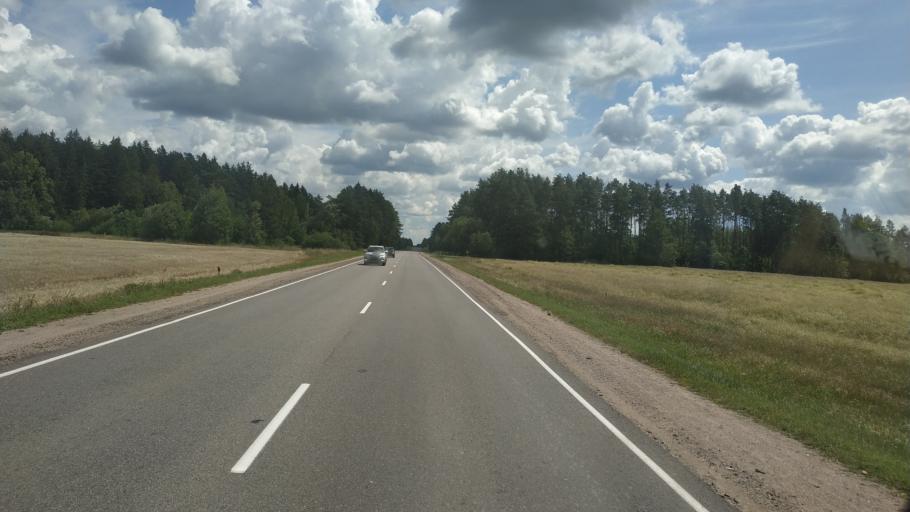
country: BY
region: Mogilev
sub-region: Mahilyowski Rayon
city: Veyno
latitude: 53.8309
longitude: 30.4071
